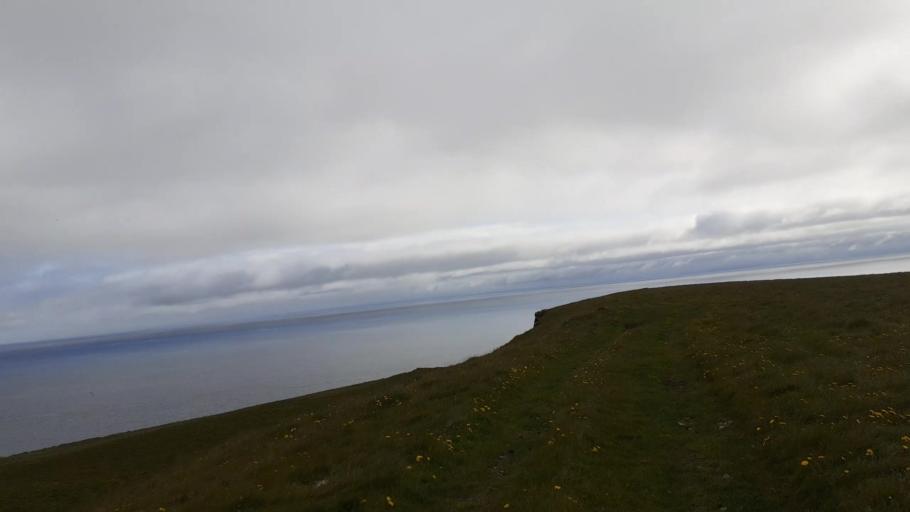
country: IS
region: Northeast
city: Dalvik
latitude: 66.5384
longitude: -17.9824
